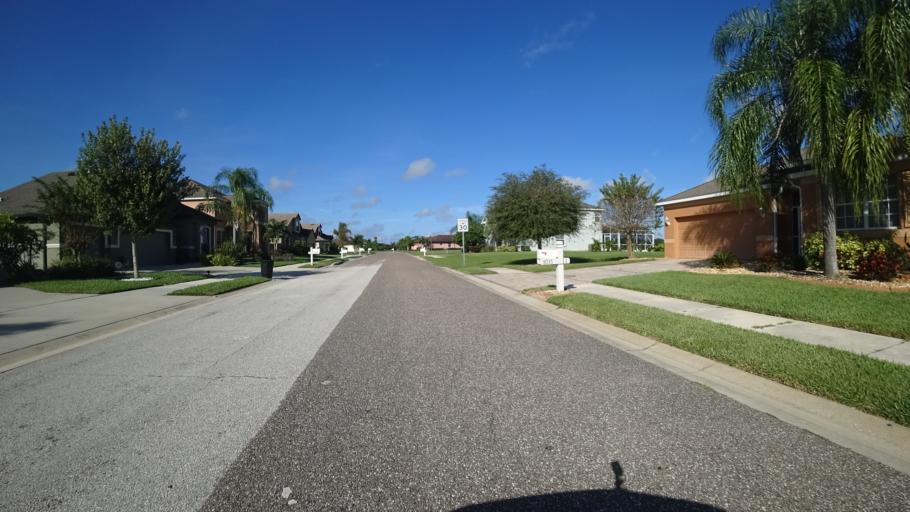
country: US
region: Florida
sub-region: Manatee County
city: Ellenton
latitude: 27.5944
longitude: -82.4952
